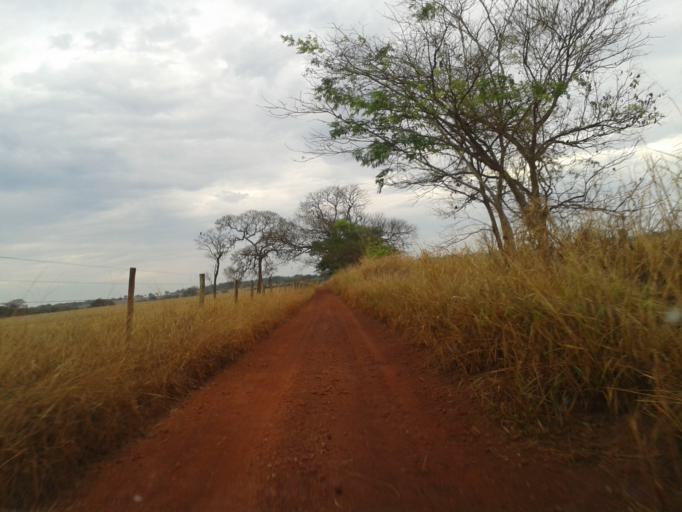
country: BR
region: Minas Gerais
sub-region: Capinopolis
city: Capinopolis
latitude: -18.8749
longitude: -49.7956
